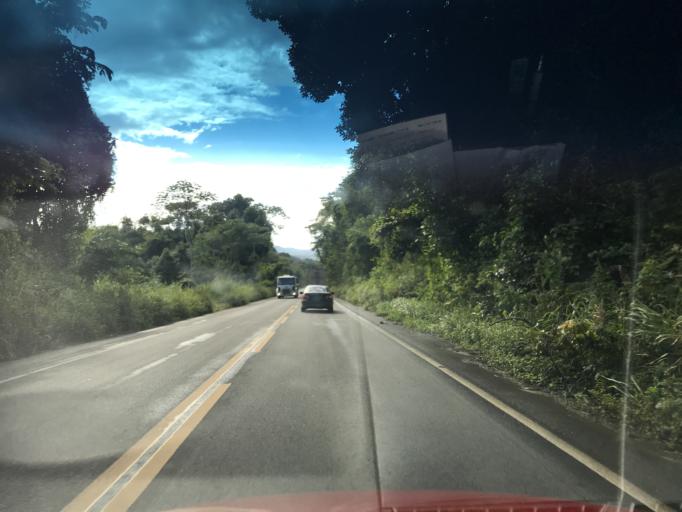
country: BR
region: Bahia
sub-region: Ibirapitanga
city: Ibirapitanga
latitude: -14.1786
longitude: -39.3209
